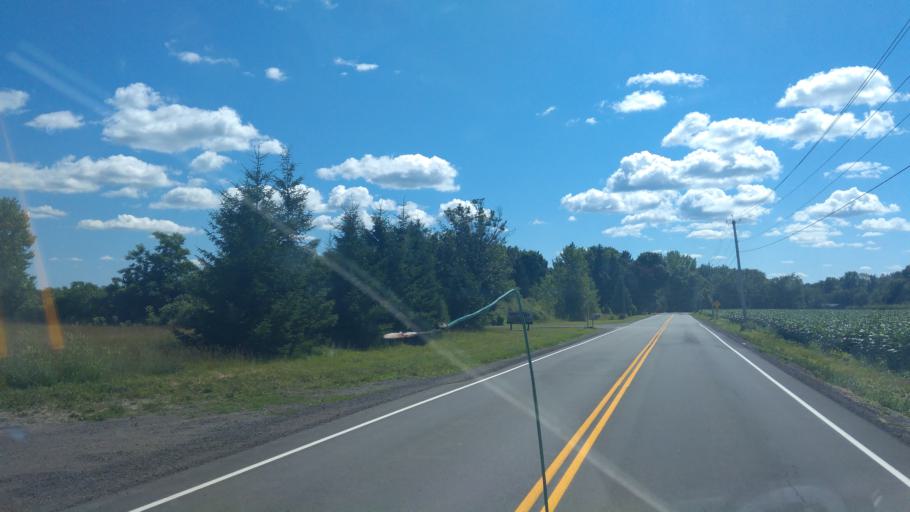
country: US
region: New York
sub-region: Wayne County
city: Sodus
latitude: 43.2023
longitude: -77.0434
